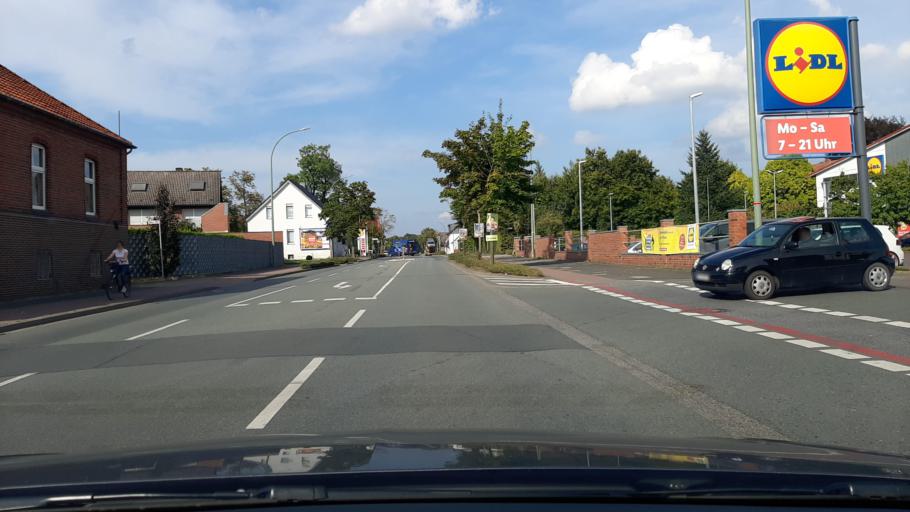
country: DE
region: North Rhine-Westphalia
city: Ahlen
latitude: 51.7750
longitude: 7.8972
